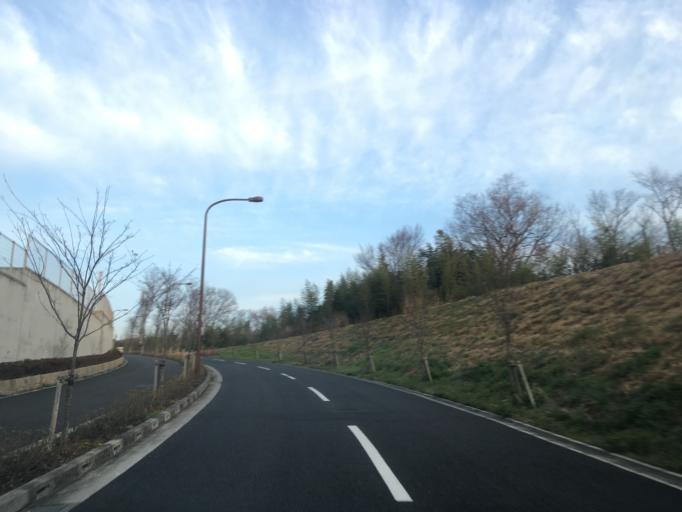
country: JP
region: Tokyo
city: Hino
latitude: 35.6356
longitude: 139.4030
